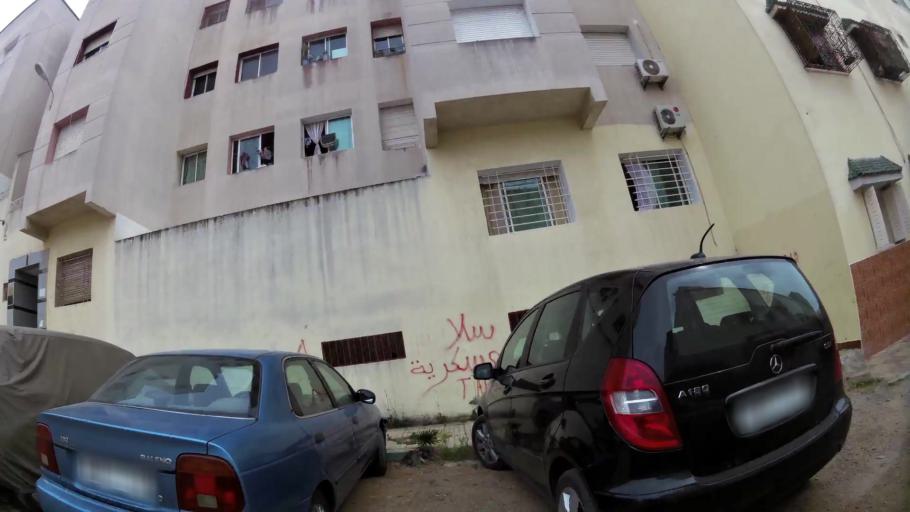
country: MA
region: Rabat-Sale-Zemmour-Zaer
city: Sale
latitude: 34.0288
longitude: -6.8041
